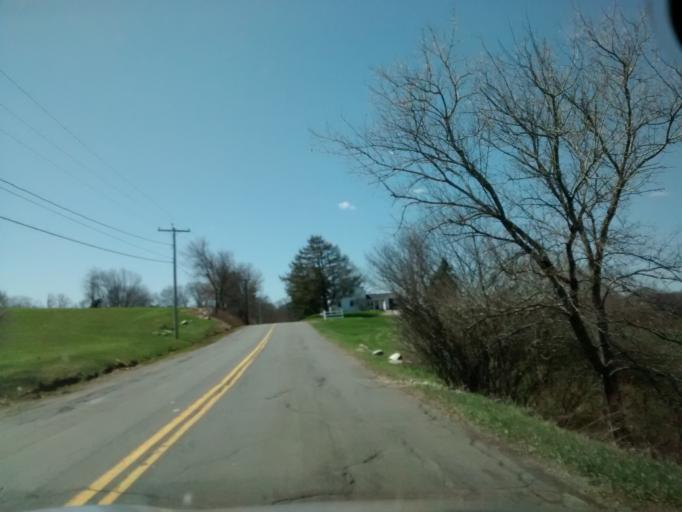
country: US
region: Massachusetts
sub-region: Worcester County
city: Sutton
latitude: 42.1132
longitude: -71.8025
